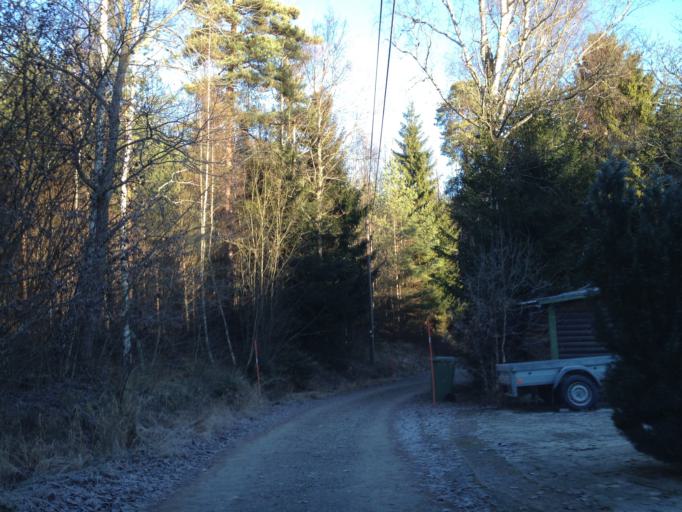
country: SE
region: Stockholm
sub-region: Sodertalje Kommun
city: Soedertaelje
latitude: 59.1631
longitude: 17.5789
